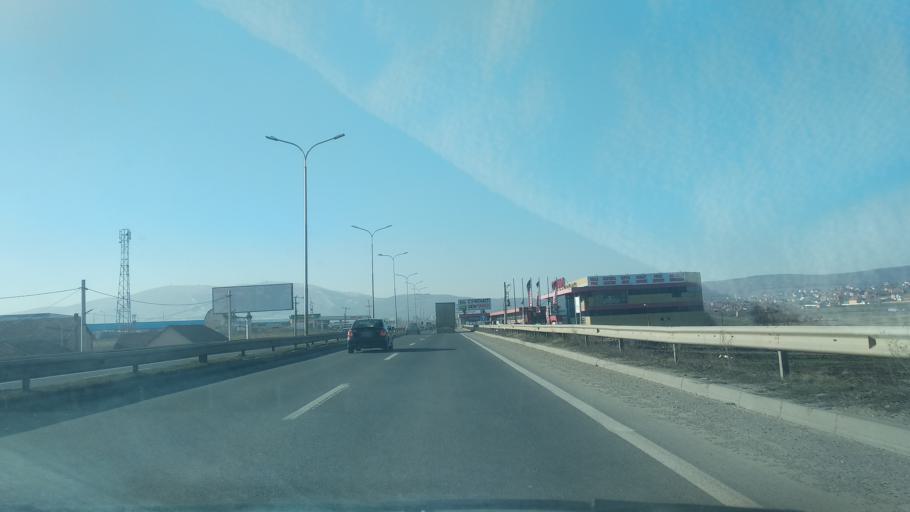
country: XK
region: Pristina
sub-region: Komuna e Gracanices
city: Glanica
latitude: 42.6034
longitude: 21.0413
